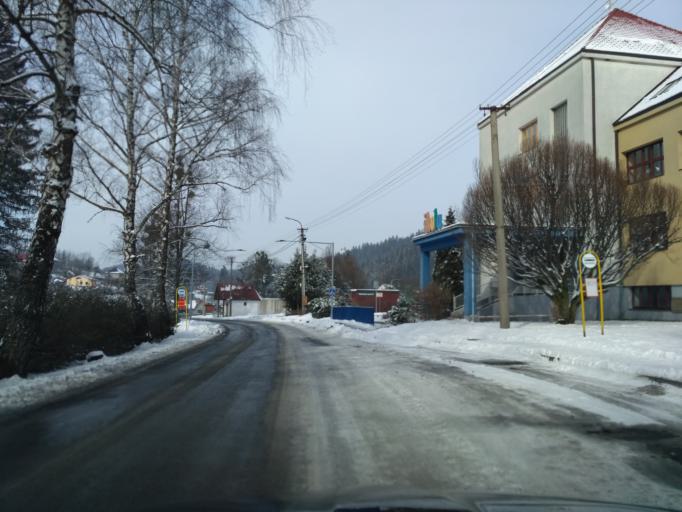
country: CZ
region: Zlin
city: Valasska Bystrice
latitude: 49.4119
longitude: 18.1124
